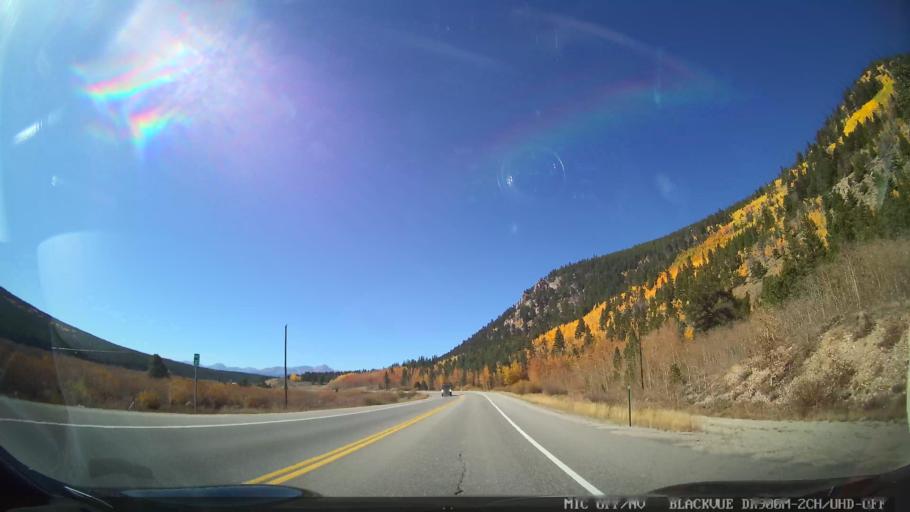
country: US
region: Colorado
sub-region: Lake County
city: Leadville North
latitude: 39.2926
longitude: -106.2772
